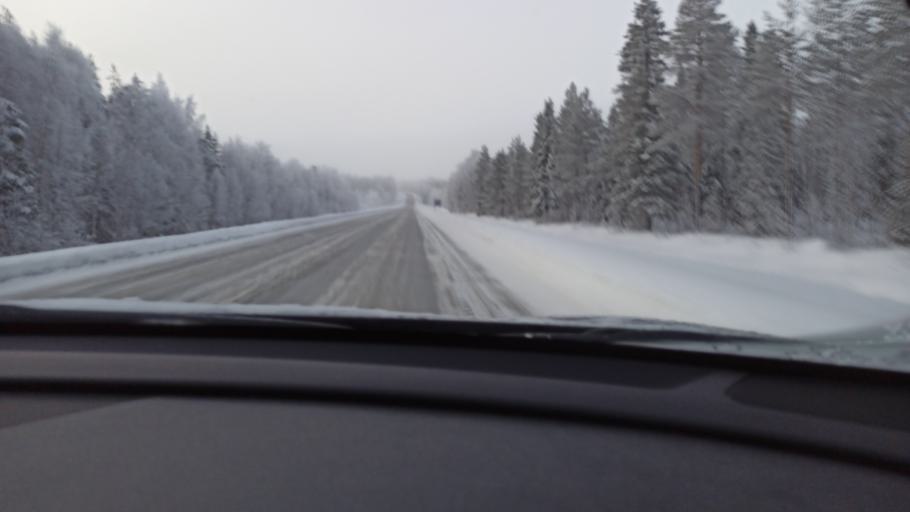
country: FI
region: Lapland
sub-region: Pohjois-Lappi
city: Sodankylae
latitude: 66.9729
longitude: 26.3081
